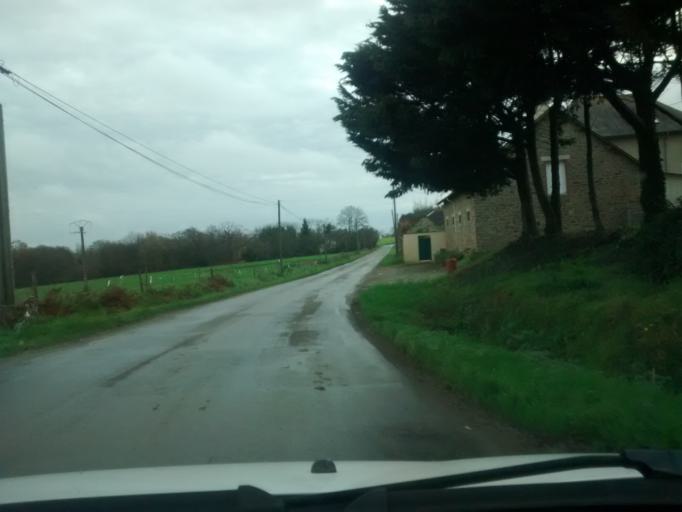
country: FR
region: Brittany
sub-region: Departement d'Ille-et-Vilaine
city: Cesson-Sevigne
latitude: 48.1419
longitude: -1.6048
